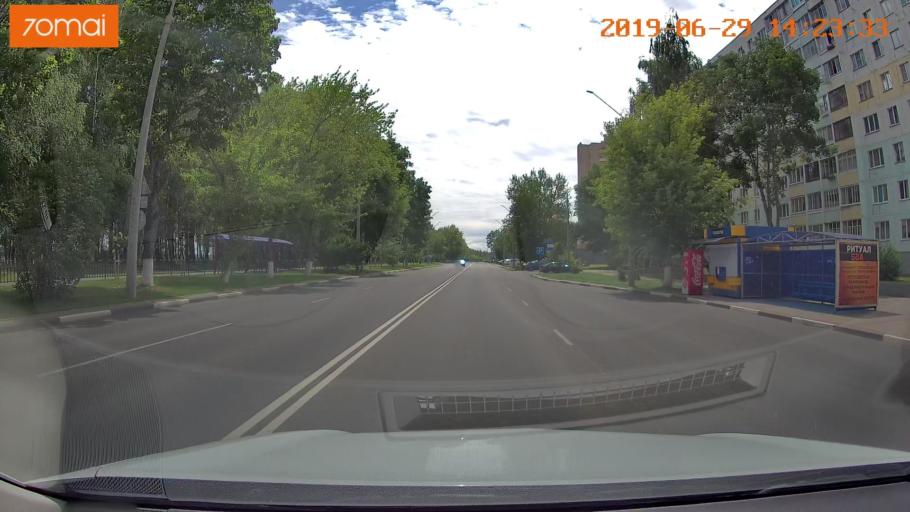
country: BY
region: Minsk
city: Salihorsk
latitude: 52.7853
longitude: 27.5539
